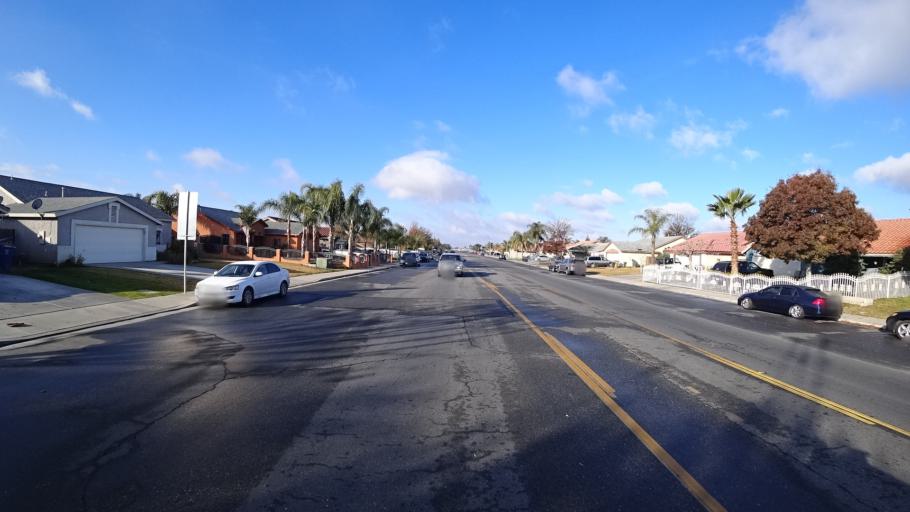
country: US
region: California
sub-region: Kern County
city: Greenfield
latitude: 35.2886
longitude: -119.0128
